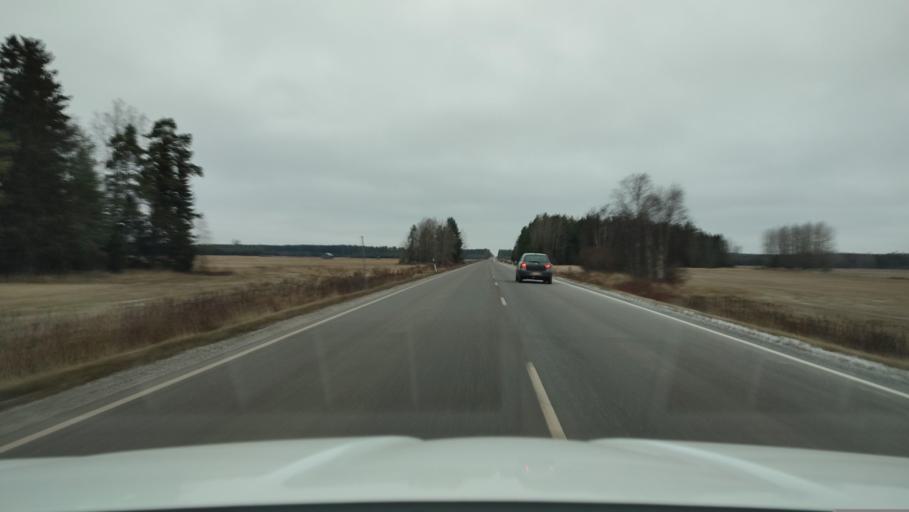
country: FI
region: Ostrobothnia
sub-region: Sydosterbotten
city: Naerpes
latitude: 62.4785
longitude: 21.4387
